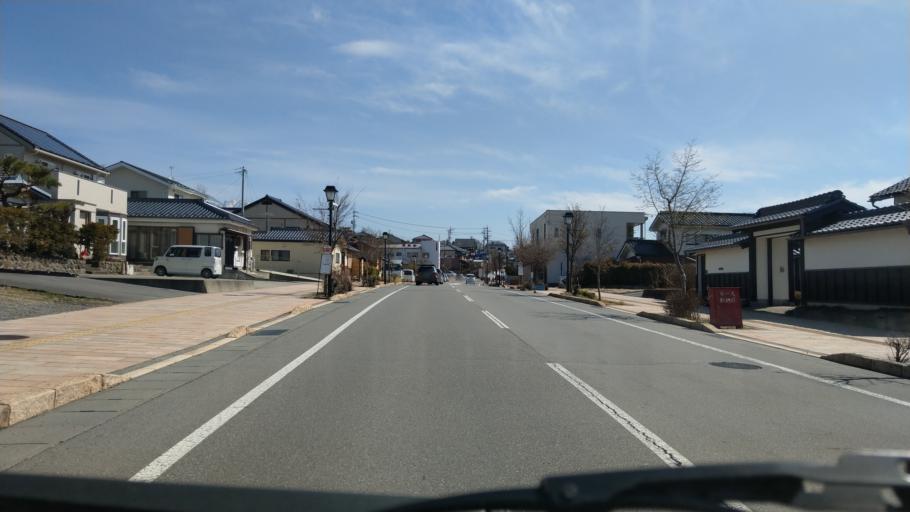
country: JP
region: Nagano
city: Ueda
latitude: 36.3552
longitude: 138.3347
